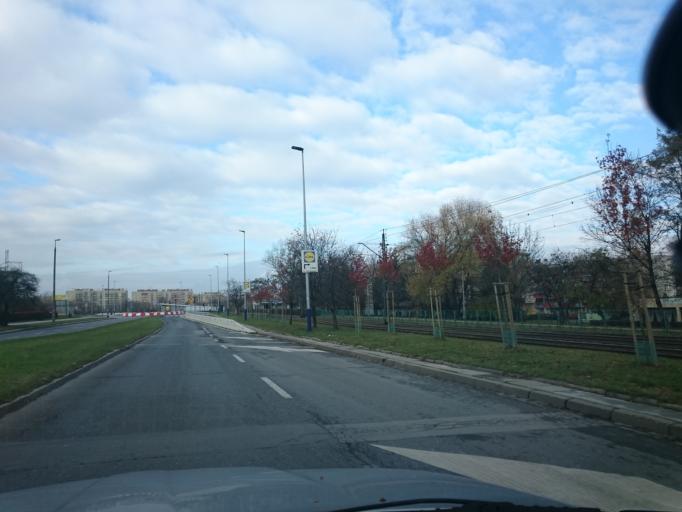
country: PL
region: Lesser Poland Voivodeship
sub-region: Powiat wielicki
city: Czarnochowice
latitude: 50.0162
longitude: 20.0184
